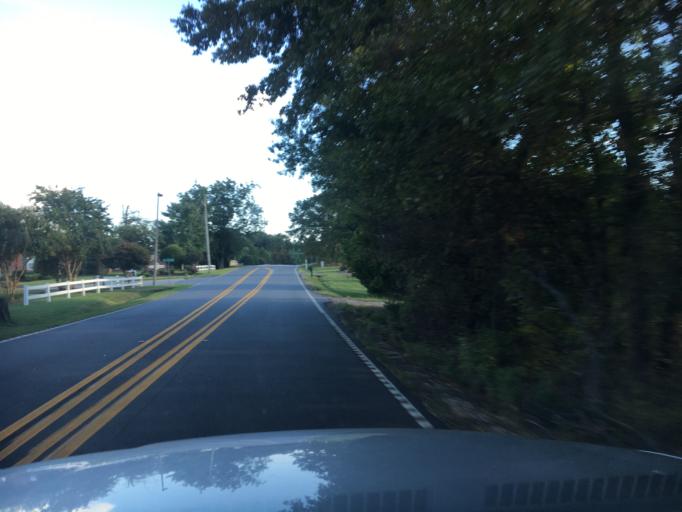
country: US
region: South Carolina
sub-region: Spartanburg County
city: Roebuck
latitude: 34.8949
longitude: -82.0071
